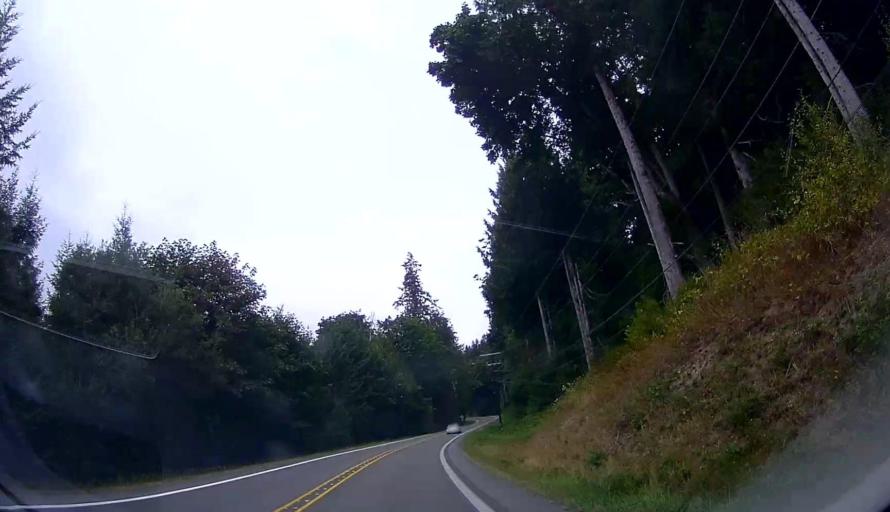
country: US
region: Washington
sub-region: Snohomish County
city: Tulalip
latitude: 48.0939
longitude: -122.3182
